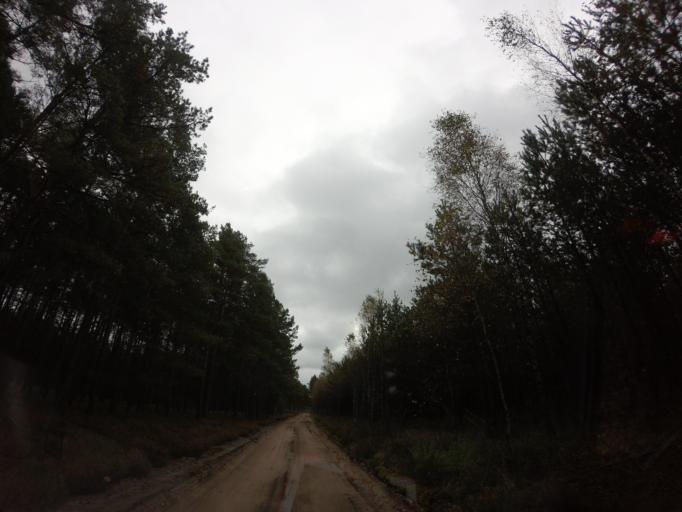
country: PL
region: West Pomeranian Voivodeship
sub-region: Powiat choszczenski
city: Drawno
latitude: 53.1350
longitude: 15.7633
